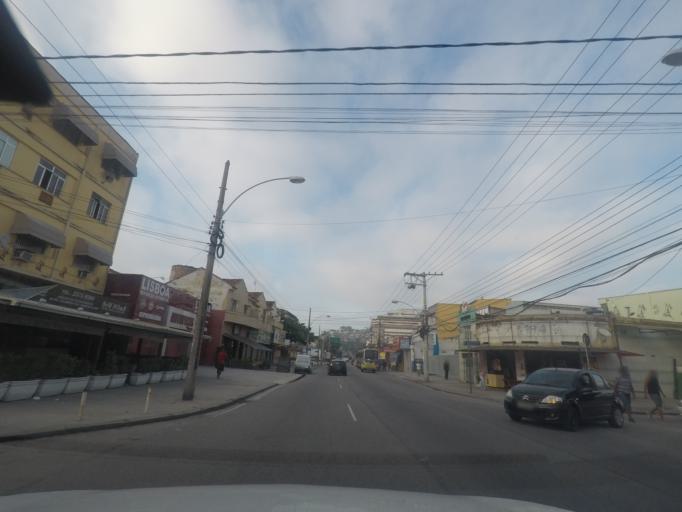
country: BR
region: Rio de Janeiro
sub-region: Duque De Caxias
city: Duque de Caxias
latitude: -22.8331
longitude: -43.2802
